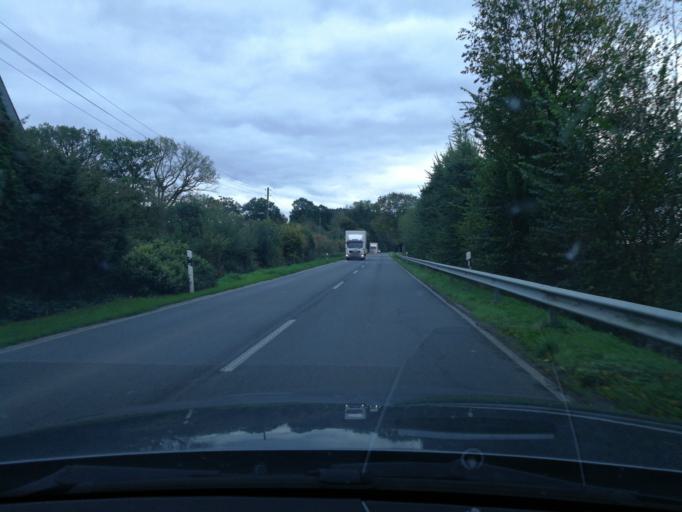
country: DE
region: North Rhine-Westphalia
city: Straelen
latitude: 51.4527
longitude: 6.2389
